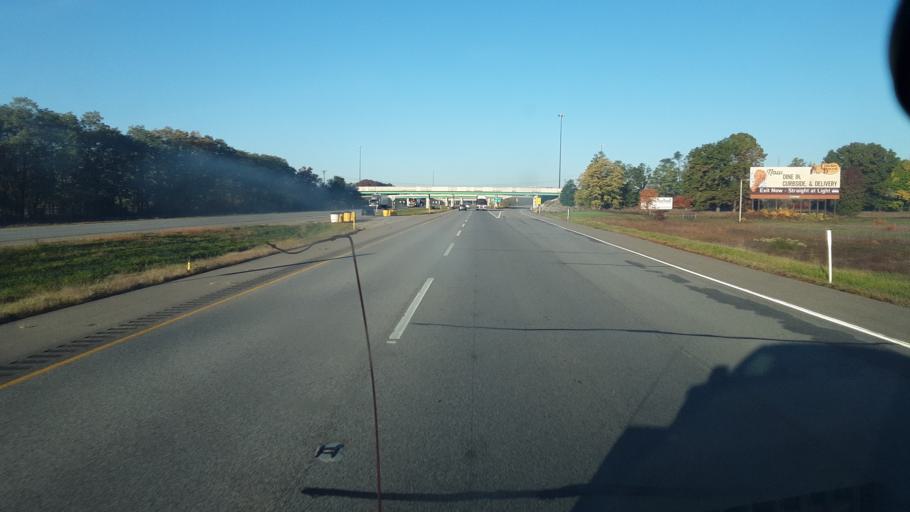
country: US
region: Indiana
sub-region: Elkhart County
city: Simonton Lake
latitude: 41.7312
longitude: -85.9628
